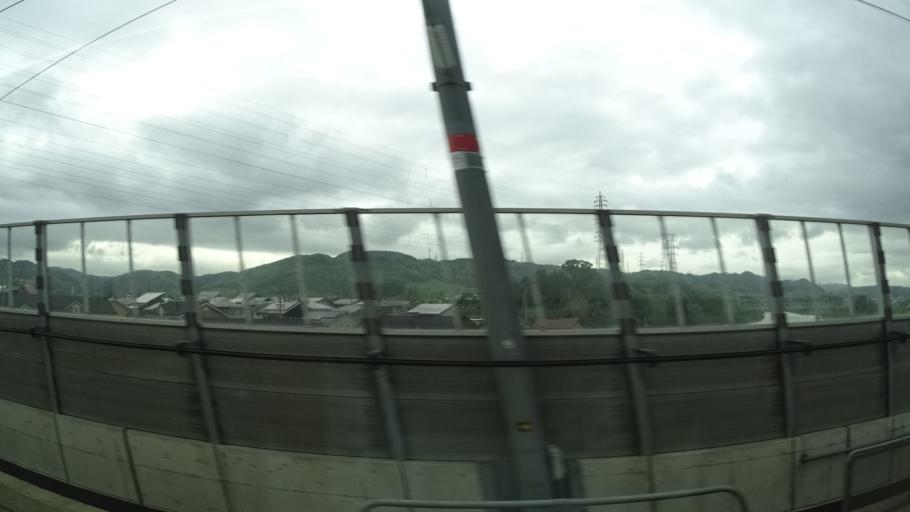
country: JP
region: Nagano
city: Nakano
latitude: 36.7235
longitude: 138.3082
